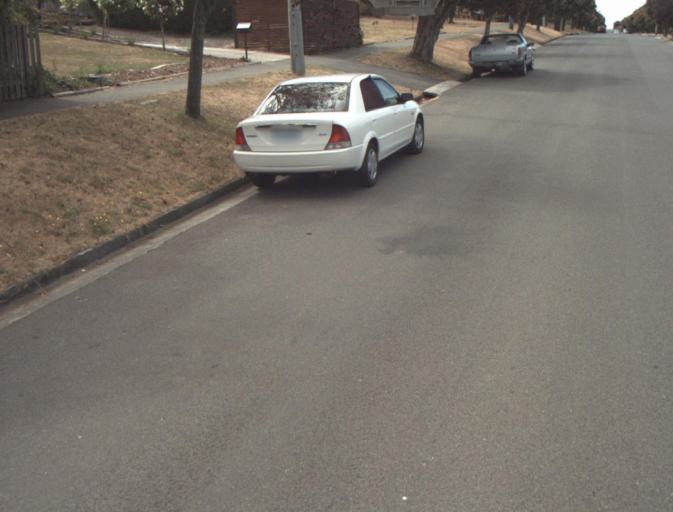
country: AU
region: Tasmania
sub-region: Launceston
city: West Launceston
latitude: -41.4558
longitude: 147.1237
